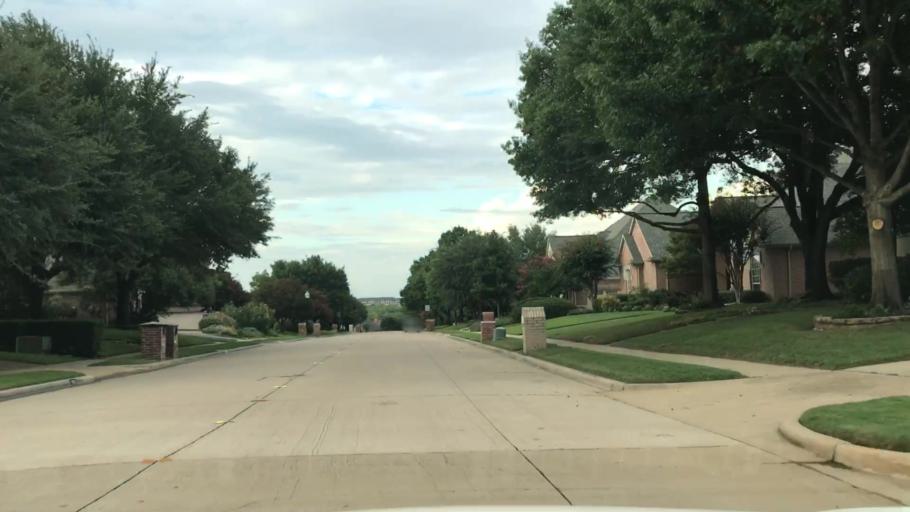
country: US
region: Texas
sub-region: Denton County
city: The Colony
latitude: 33.0398
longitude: -96.8501
